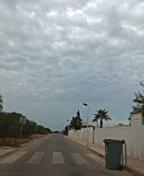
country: ES
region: Murcia
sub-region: Murcia
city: San Pedro del Pinatar
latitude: 37.7776
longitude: -0.7526
